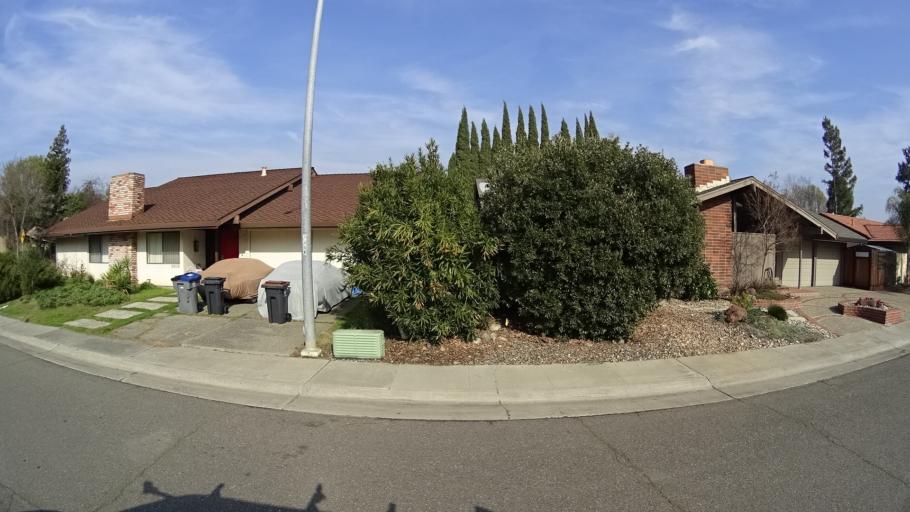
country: US
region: California
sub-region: Yolo County
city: Davis
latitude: 38.5681
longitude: -121.7563
